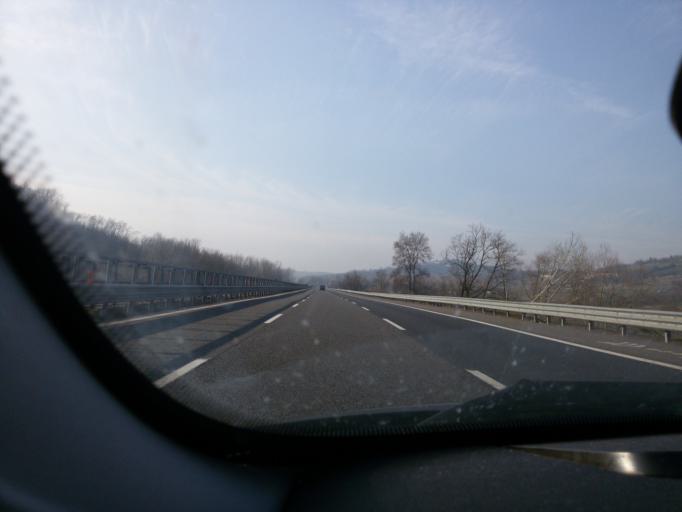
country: IT
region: Piedmont
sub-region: Provincia di Alessandria
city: Castelletto Monferrato
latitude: 44.9771
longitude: 8.5468
